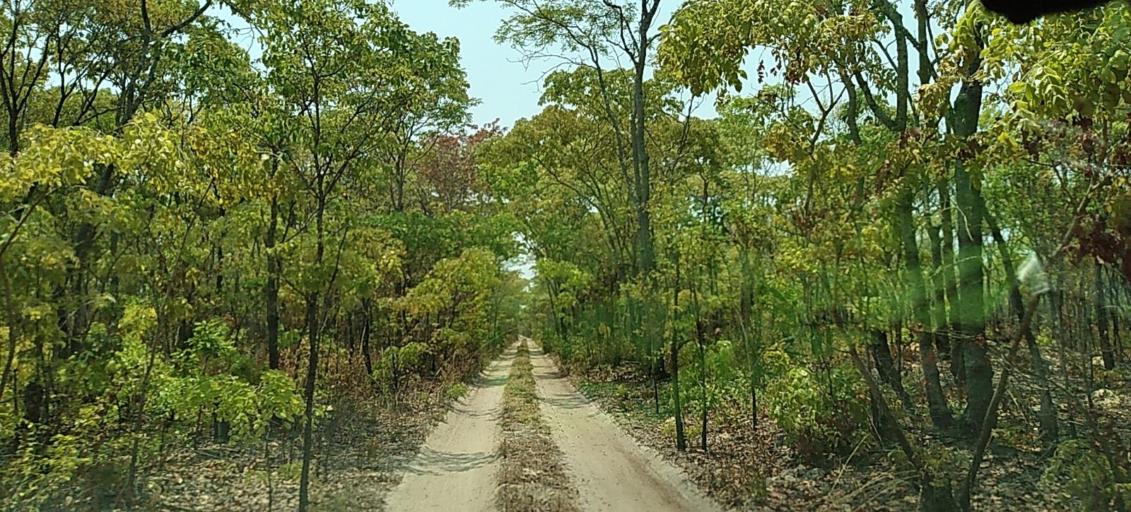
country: ZM
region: North-Western
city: Kabompo
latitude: -13.6515
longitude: 24.4721
